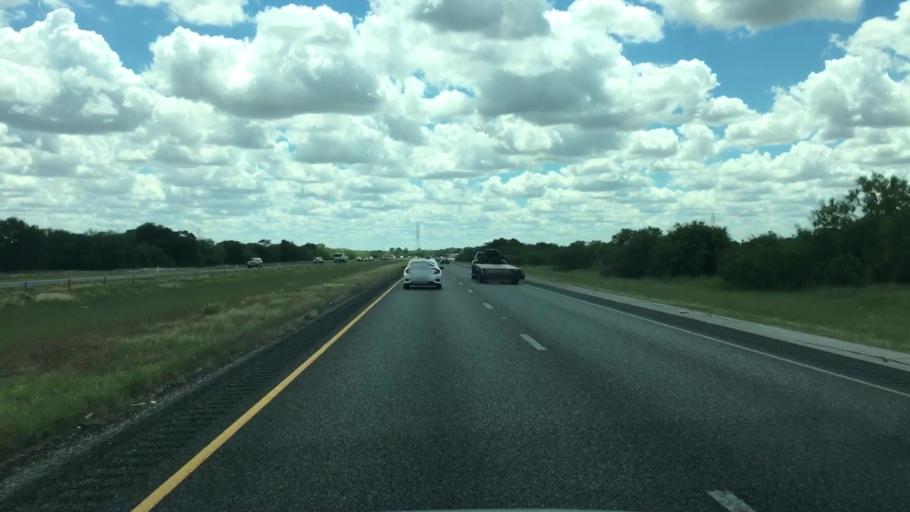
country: US
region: Texas
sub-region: Bexar County
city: Elmendorf
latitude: 29.2583
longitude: -98.3953
